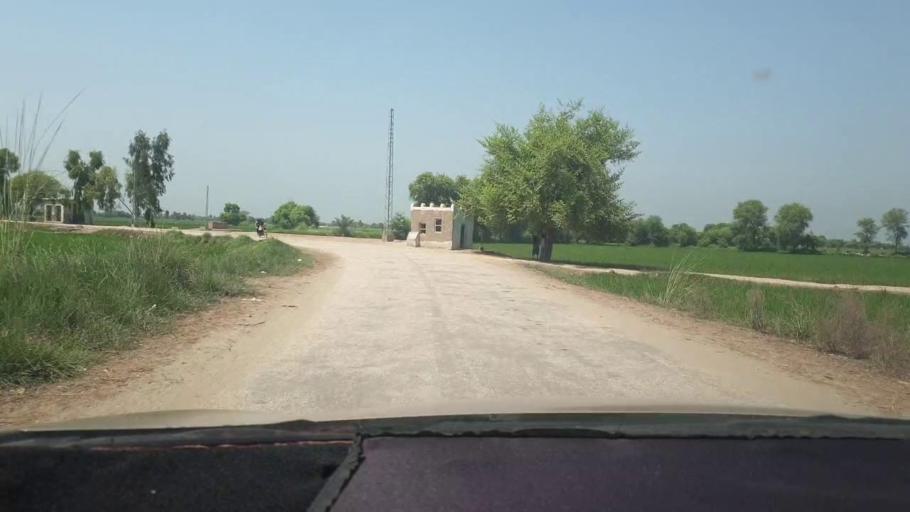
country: PK
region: Sindh
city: Miro Khan
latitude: 27.6715
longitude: 68.0597
